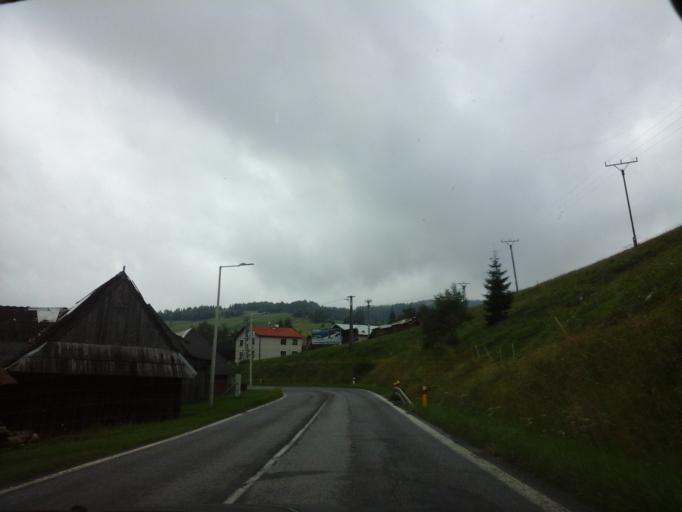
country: SK
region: Presovsky
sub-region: Okres Poprad
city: Zdiar
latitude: 49.2702
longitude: 20.2811
